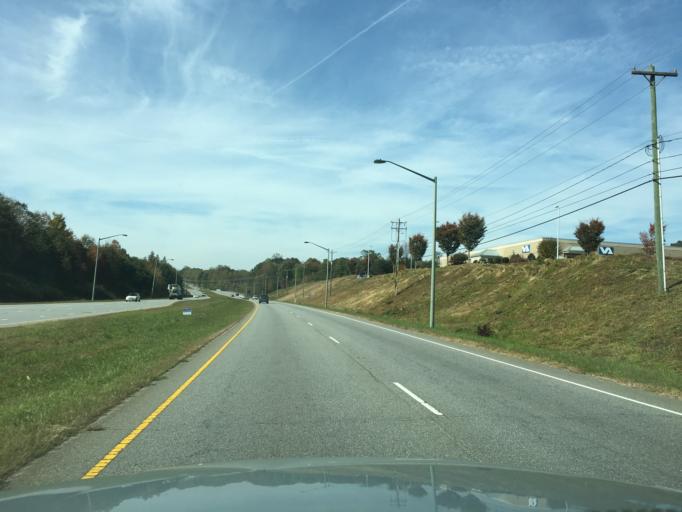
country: US
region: North Carolina
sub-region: Catawba County
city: Saint Stephens
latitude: 35.7246
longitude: -81.2850
